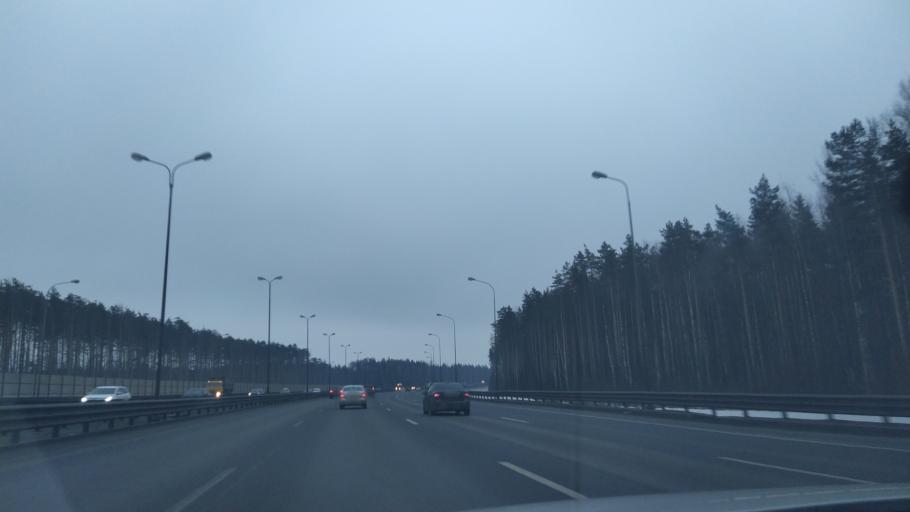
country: RU
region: St.-Petersburg
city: Krasnogvargeisky
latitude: 59.9719
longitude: 30.5470
